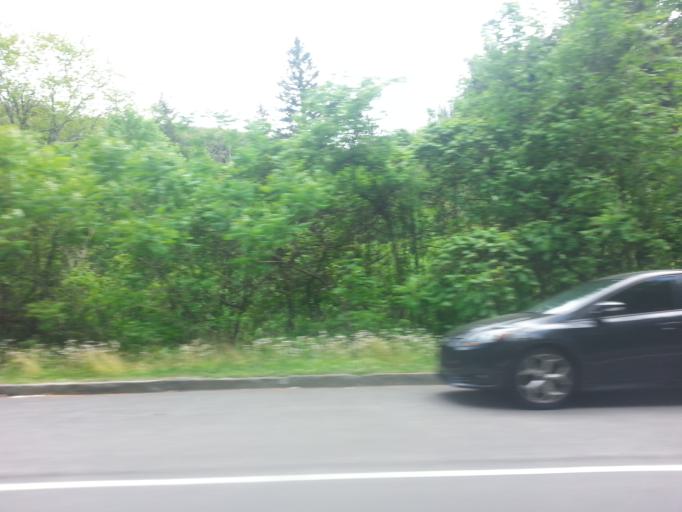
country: US
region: Tennessee
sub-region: Sevier County
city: Gatlinburg
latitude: 35.6349
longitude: -83.4678
